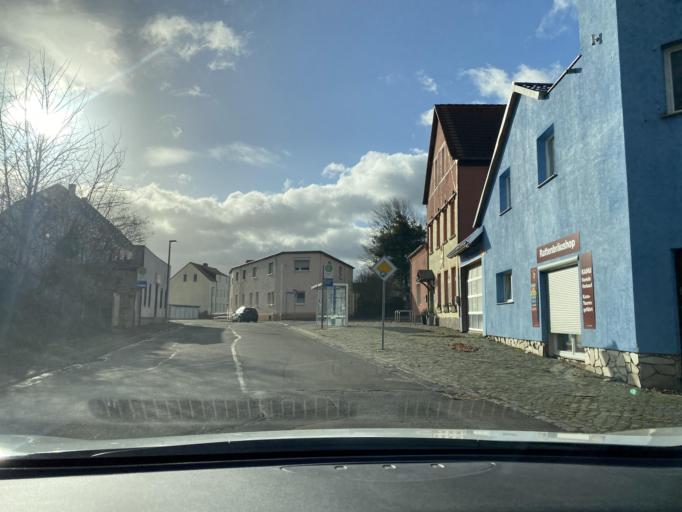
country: DE
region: Saxony
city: Zwenkau
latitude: 51.2657
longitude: 12.3089
